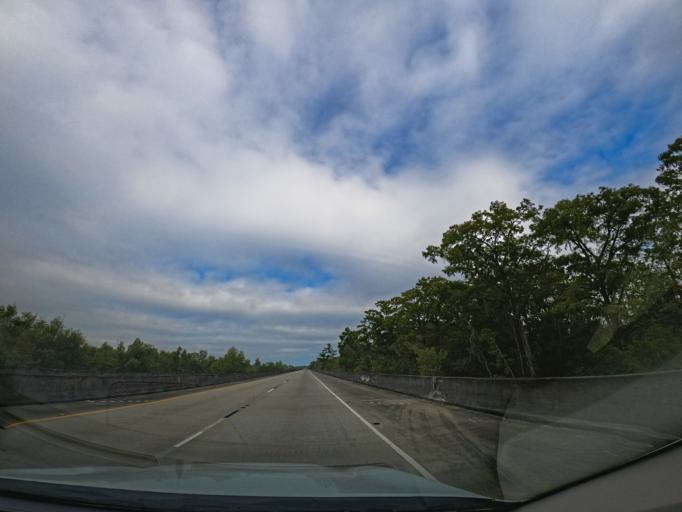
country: US
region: Louisiana
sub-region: Saint Mary Parish
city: Amelia
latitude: 29.6823
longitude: -91.1394
